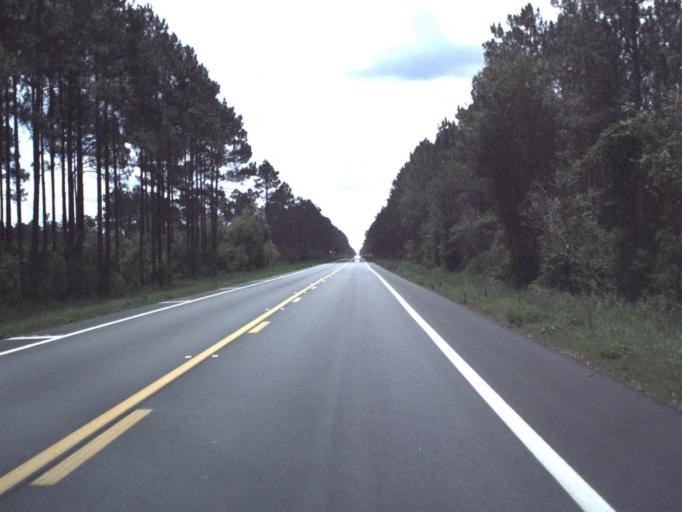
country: US
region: Florida
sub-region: Baker County
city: Macclenny
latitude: 30.5631
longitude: -82.3907
